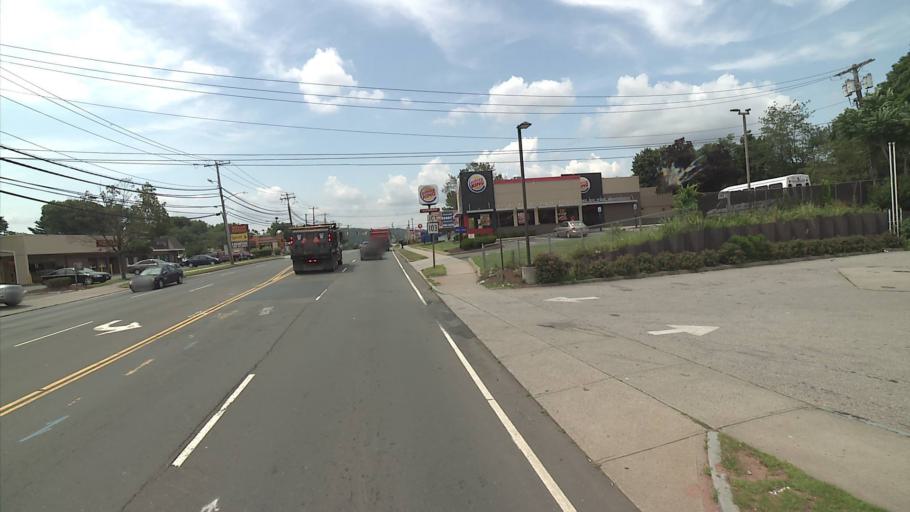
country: US
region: Connecticut
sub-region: New Haven County
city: East Haven
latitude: 41.3204
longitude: -72.8722
